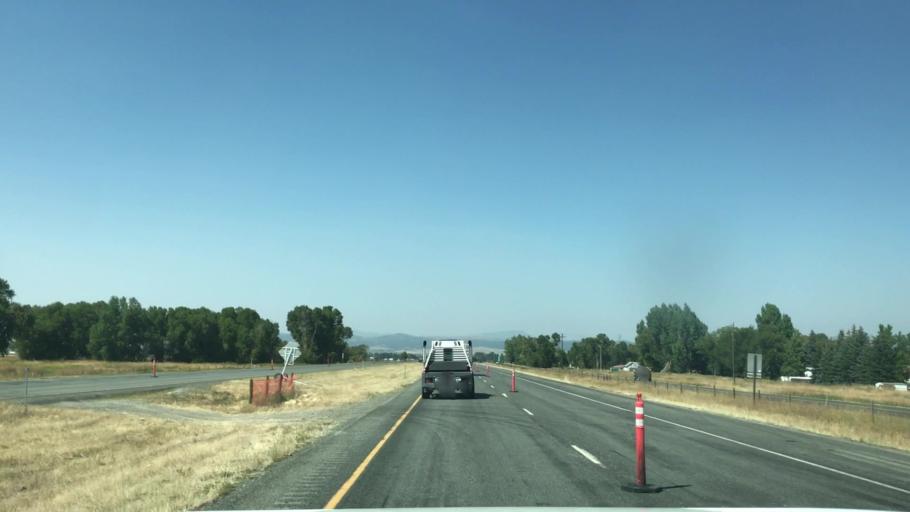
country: US
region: Montana
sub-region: Lewis and Clark County
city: Helena Valley West Central
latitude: 46.6434
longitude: -112.0111
